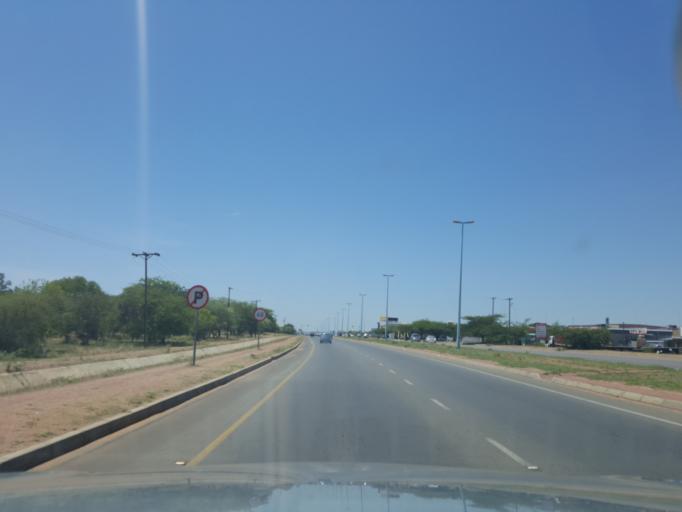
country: BW
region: Kweneng
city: Mogoditshane
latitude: -24.6036
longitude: 25.8558
